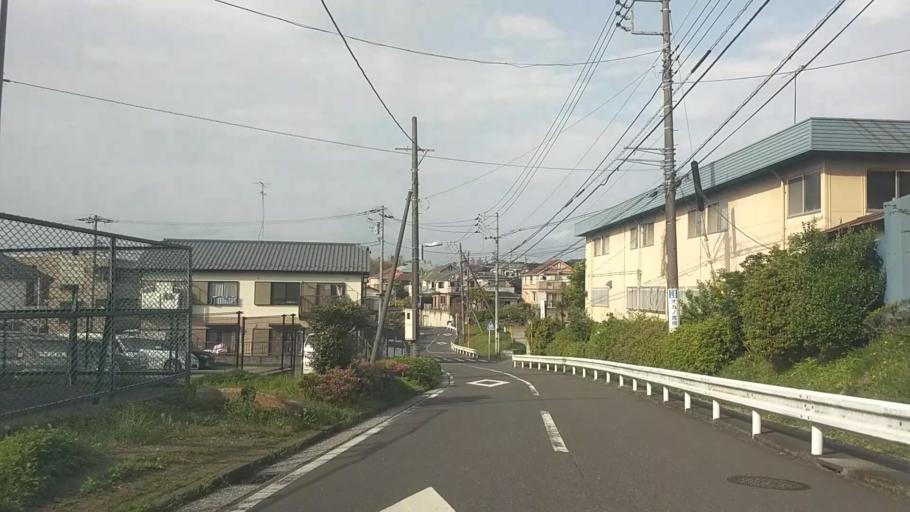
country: JP
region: Kanagawa
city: Kamakura
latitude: 35.3603
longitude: 139.5567
